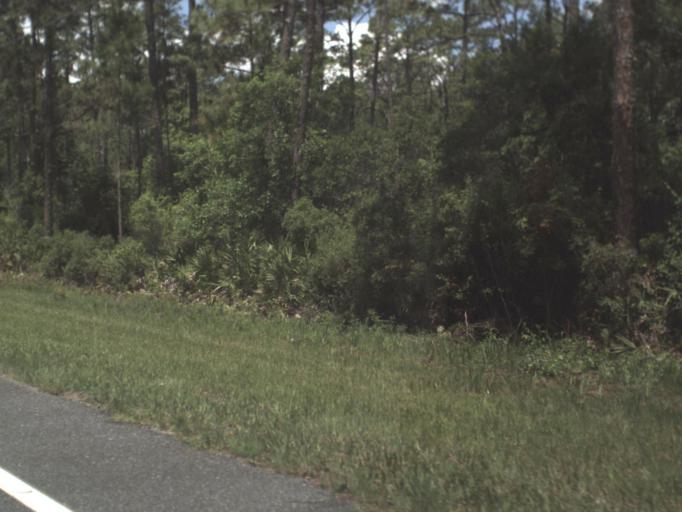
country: US
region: Florida
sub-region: Levy County
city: Williston Highlands
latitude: 29.1986
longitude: -82.6101
